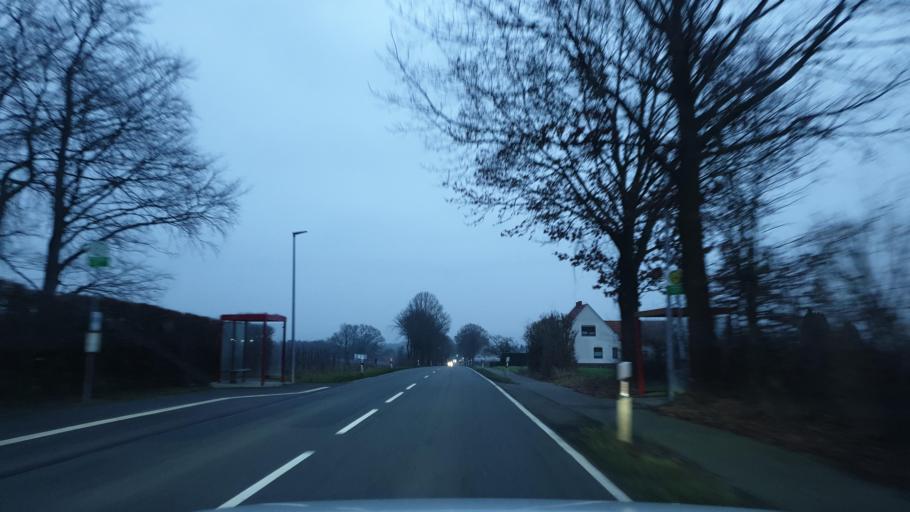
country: DE
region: North Rhine-Westphalia
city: Bad Oeynhausen
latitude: 52.2606
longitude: 8.7773
